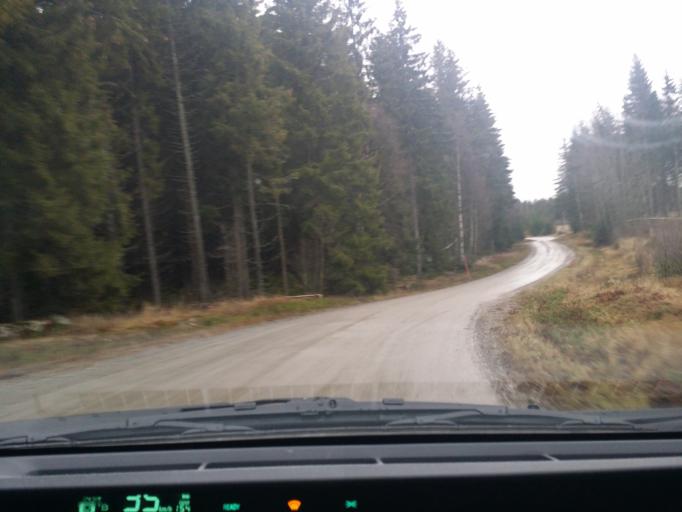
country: SE
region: Vaestmanland
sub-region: Surahammars Kommun
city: Surahammar
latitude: 59.7652
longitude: 16.2940
